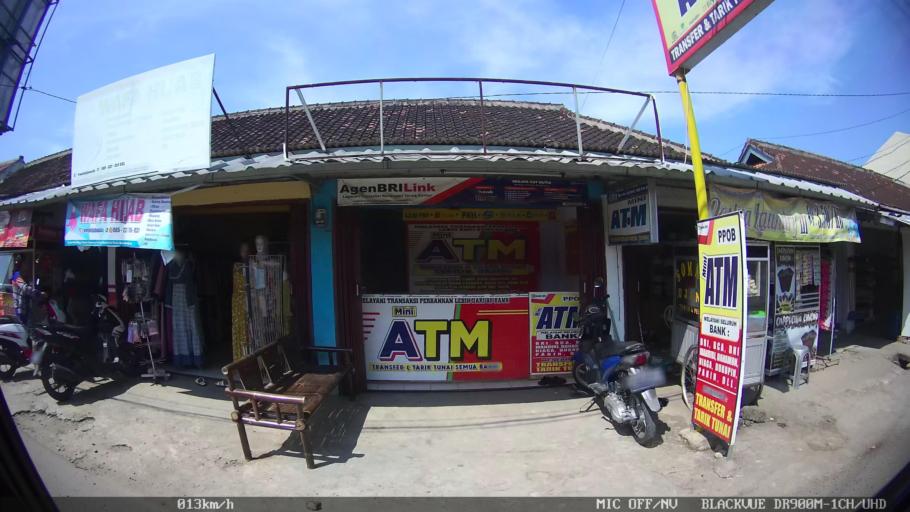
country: ID
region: Lampung
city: Kedaton
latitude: -5.3638
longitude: 105.2469
